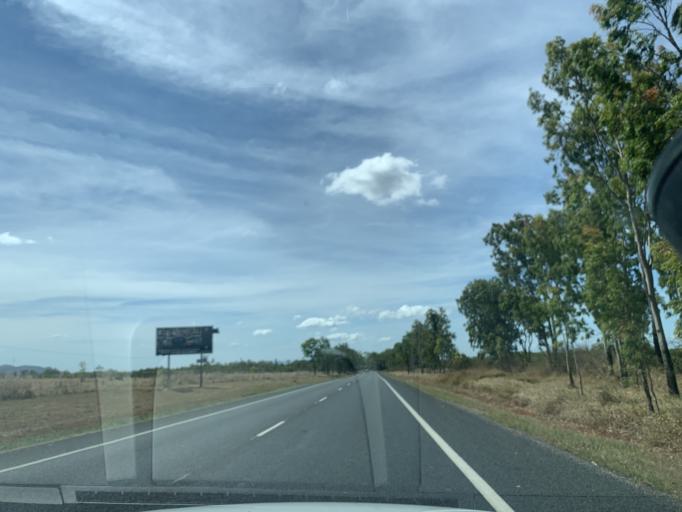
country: AU
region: Queensland
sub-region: Tablelands
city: Tolga
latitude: -17.1890
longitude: 145.4681
